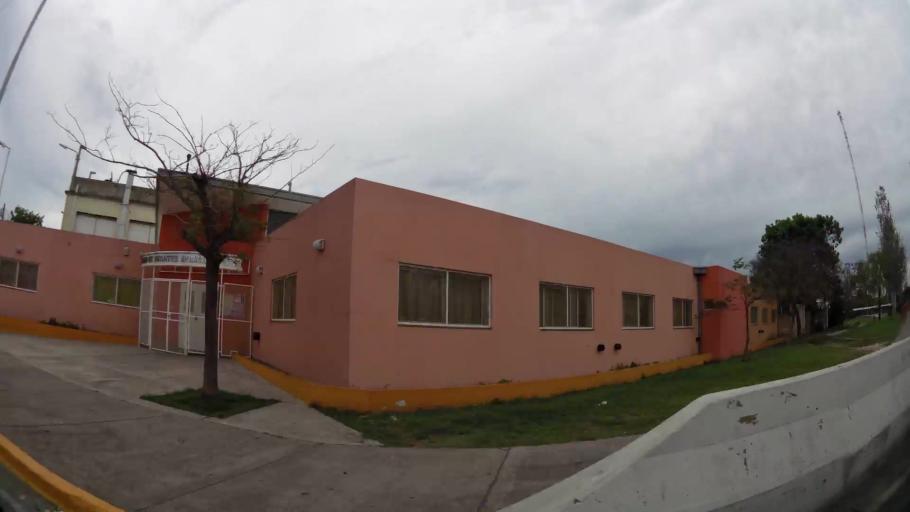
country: AR
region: Buenos Aires
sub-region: Partido de Avellaneda
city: Avellaneda
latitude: -34.6815
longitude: -58.3777
